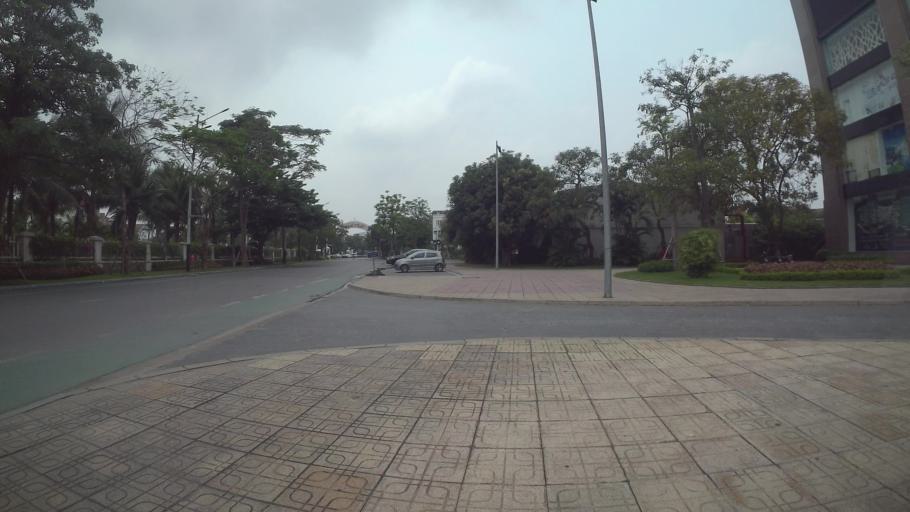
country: VN
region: Ha Noi
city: Trau Quy
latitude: 21.0507
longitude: 105.9159
